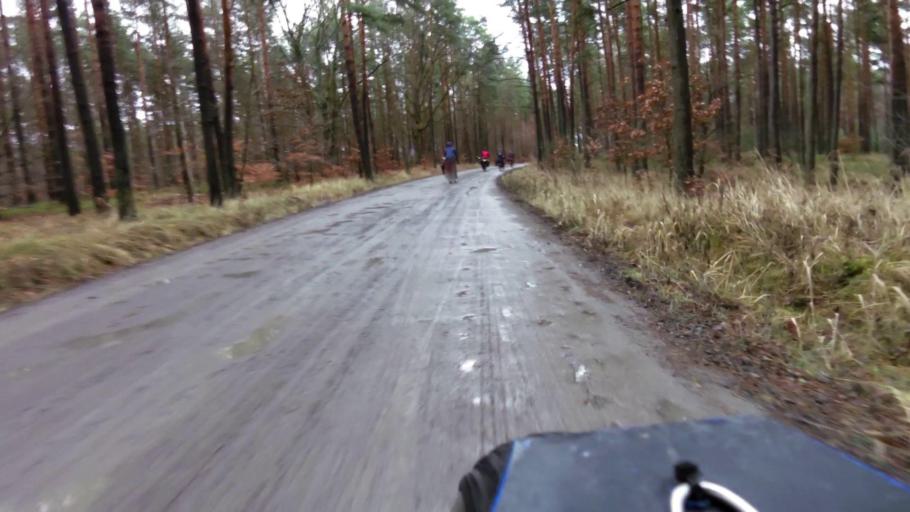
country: PL
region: Lubusz
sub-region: Powiat gorzowski
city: Witnica
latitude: 52.7049
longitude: 14.8293
